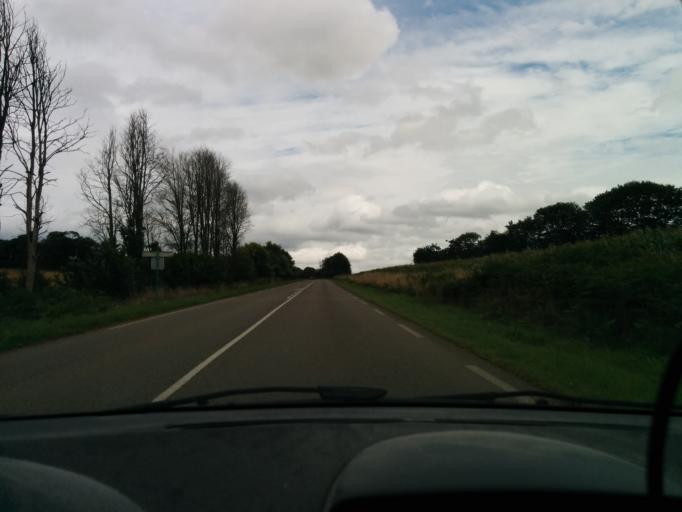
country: FR
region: Brittany
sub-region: Departement du Finistere
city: Pleyben
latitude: 48.2385
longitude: -3.9629
